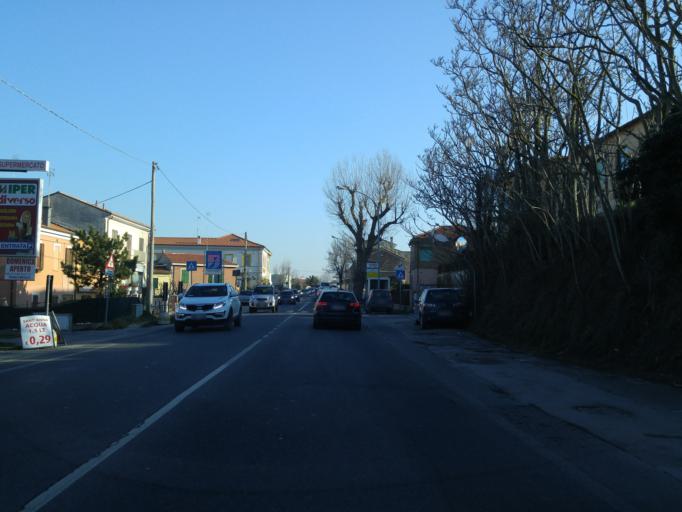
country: IT
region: The Marches
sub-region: Provincia di Pesaro e Urbino
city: Fano
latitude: 43.8539
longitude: 13.0036
